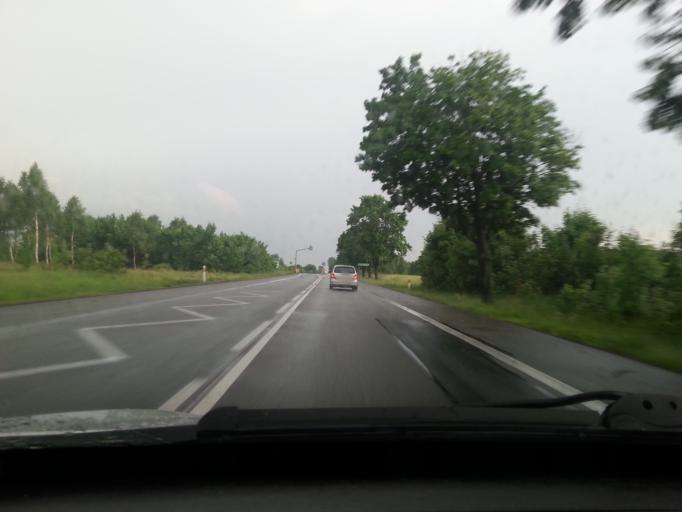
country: PL
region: Lodz Voivodeship
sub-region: Powiat zgierski
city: Strykow
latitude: 51.8581
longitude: 19.5651
